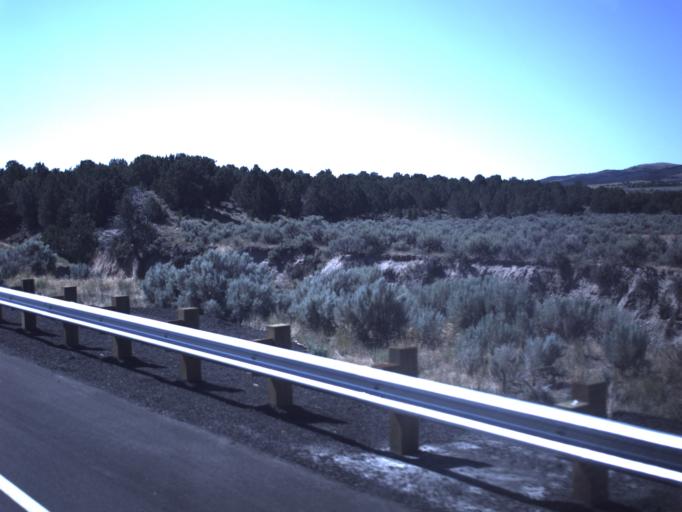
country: US
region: Utah
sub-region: Utah County
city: Eagle Mountain
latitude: 39.9887
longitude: -112.2660
